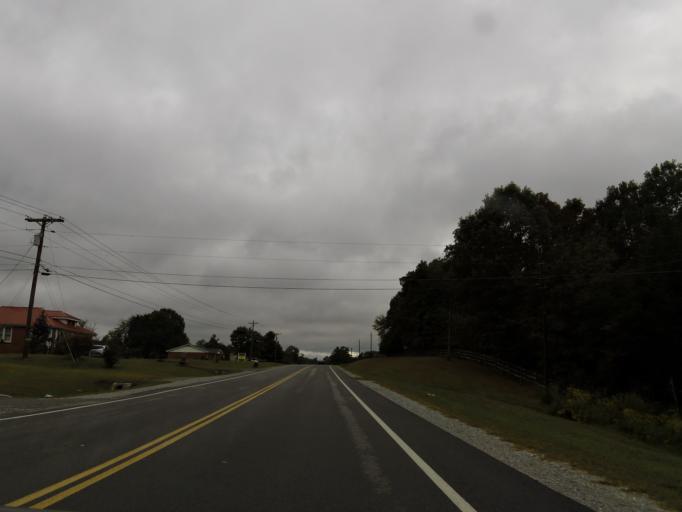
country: US
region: Tennessee
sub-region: Hamilton County
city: Lakesite
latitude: 35.1587
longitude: -85.0369
